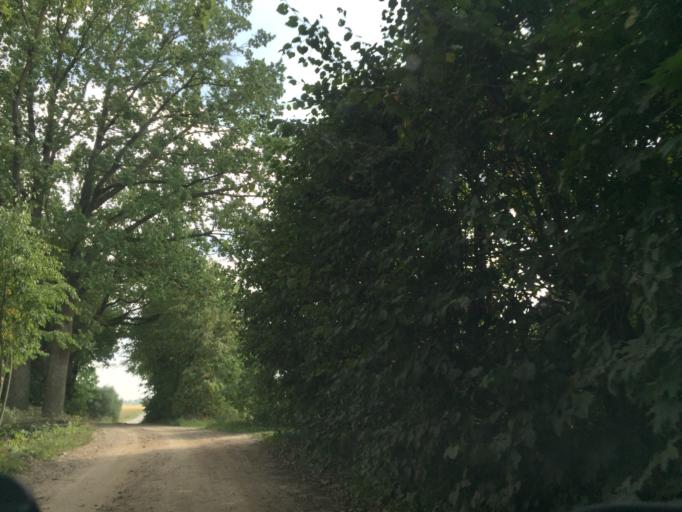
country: LV
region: Jelgava
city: Jelgava
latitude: 56.5031
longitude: 23.7567
